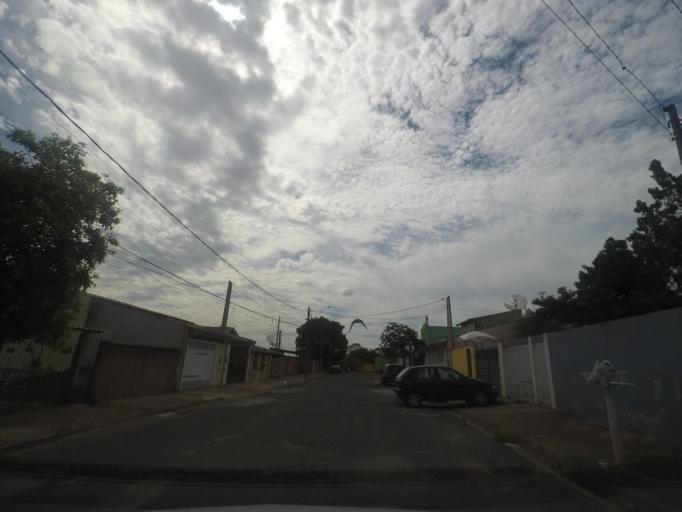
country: BR
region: Sao Paulo
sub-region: Sumare
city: Sumare
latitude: -22.8098
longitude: -47.2702
